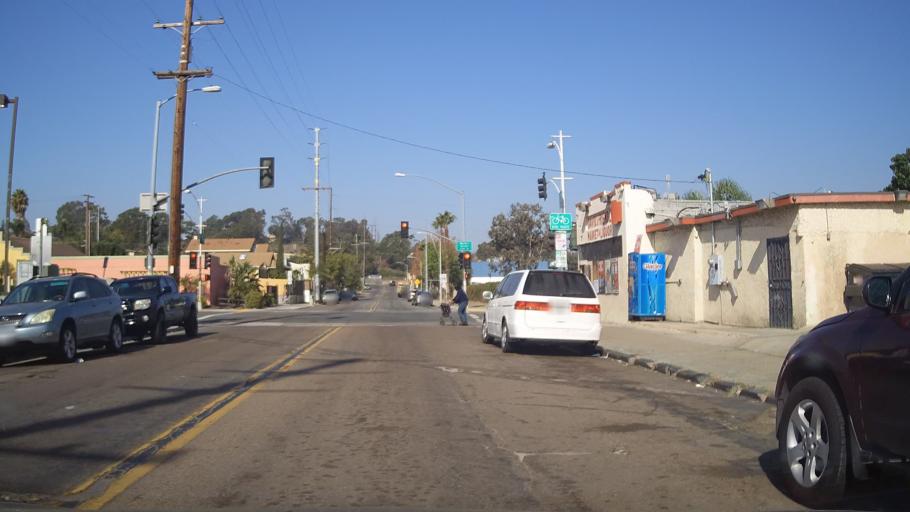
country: US
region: California
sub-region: San Diego County
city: San Diego
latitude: 32.7110
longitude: -117.1254
